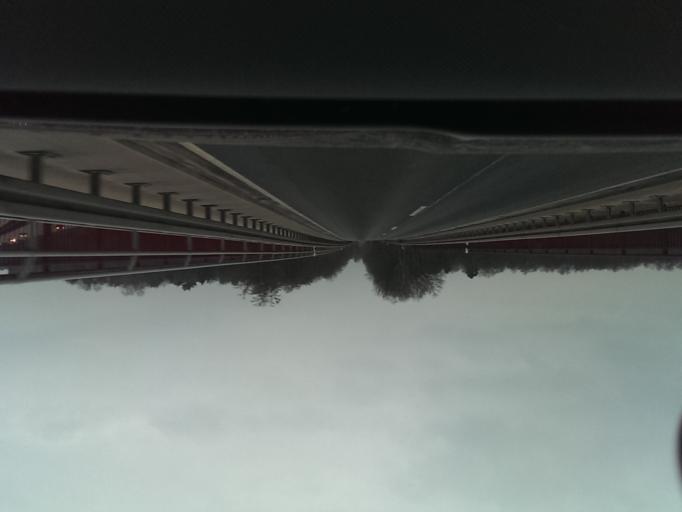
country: DE
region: Lower Saxony
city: Isernhagen Farster Bauerschaft
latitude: 52.5042
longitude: 9.8253
